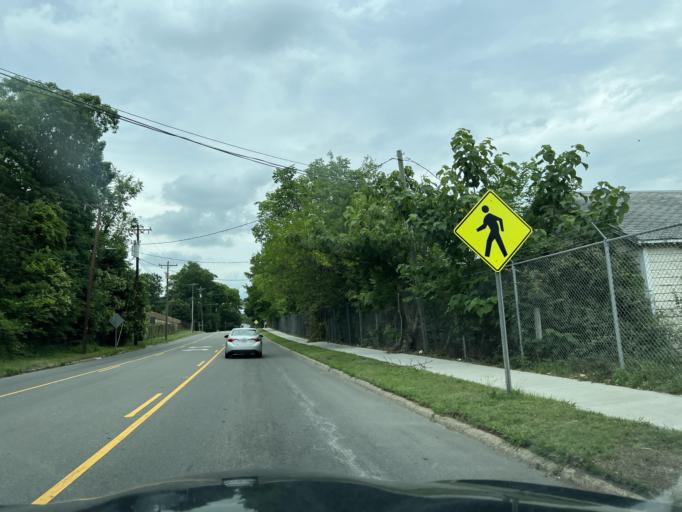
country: US
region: North Carolina
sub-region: Durham County
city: Durham
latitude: 35.9958
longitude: -78.8859
